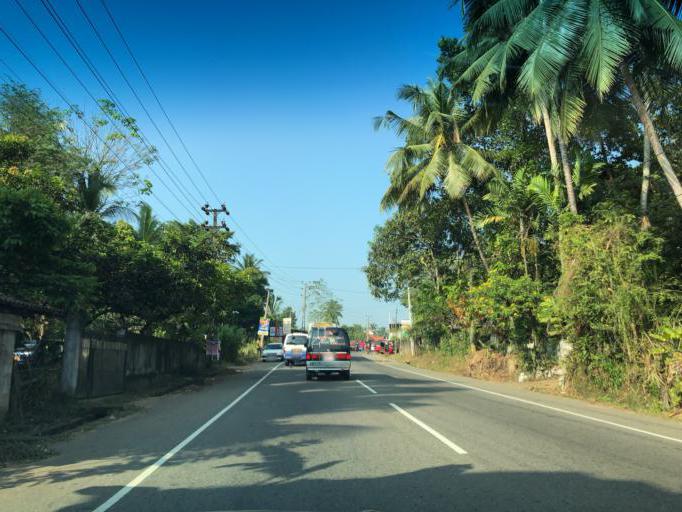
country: LK
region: Western
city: Horana South
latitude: 6.7240
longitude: 80.0844
